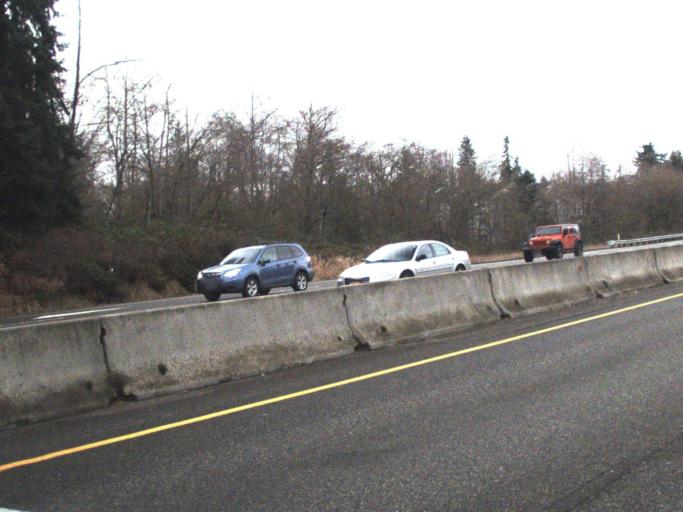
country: US
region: Washington
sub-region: Snohomish County
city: Mukilteo
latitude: 47.9231
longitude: -122.2555
